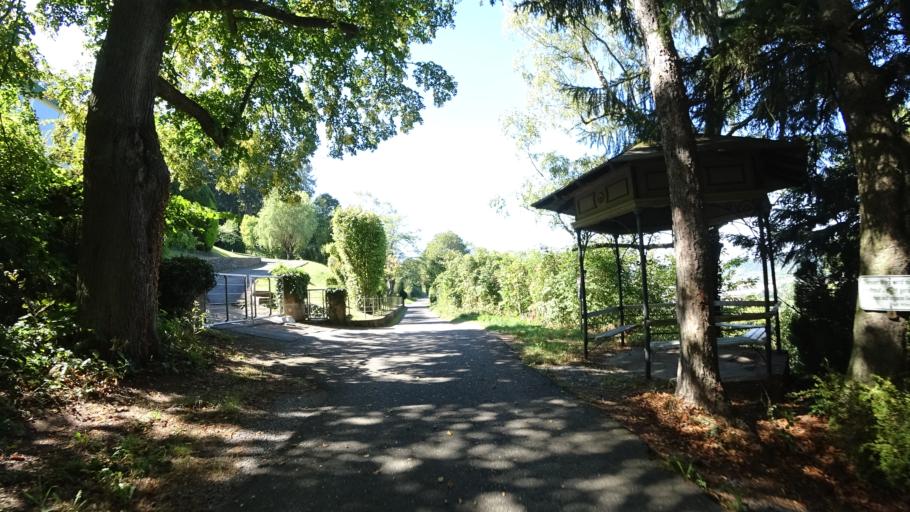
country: DE
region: Bavaria
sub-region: Regierungsbezirk Unterfranken
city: Miltenberg
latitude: 49.6972
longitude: 9.2623
